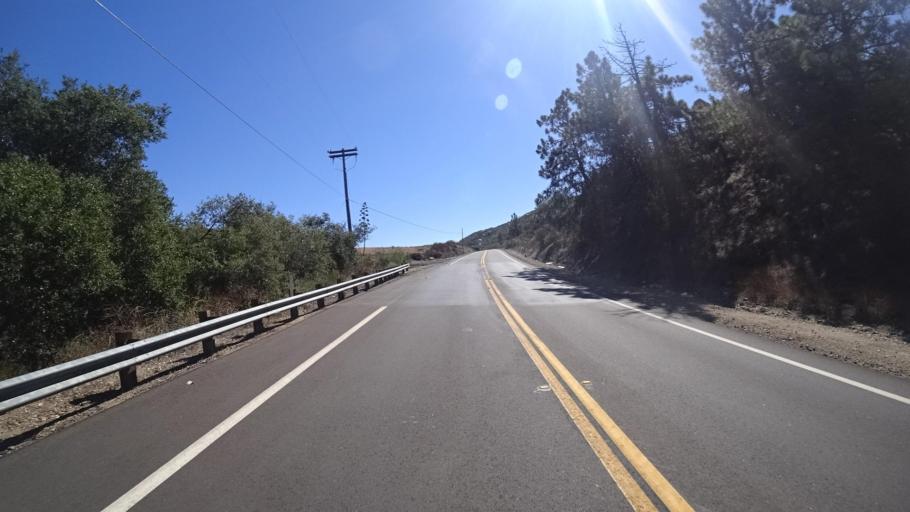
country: US
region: California
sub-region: San Diego County
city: Jamul
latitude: 32.7338
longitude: -116.7994
